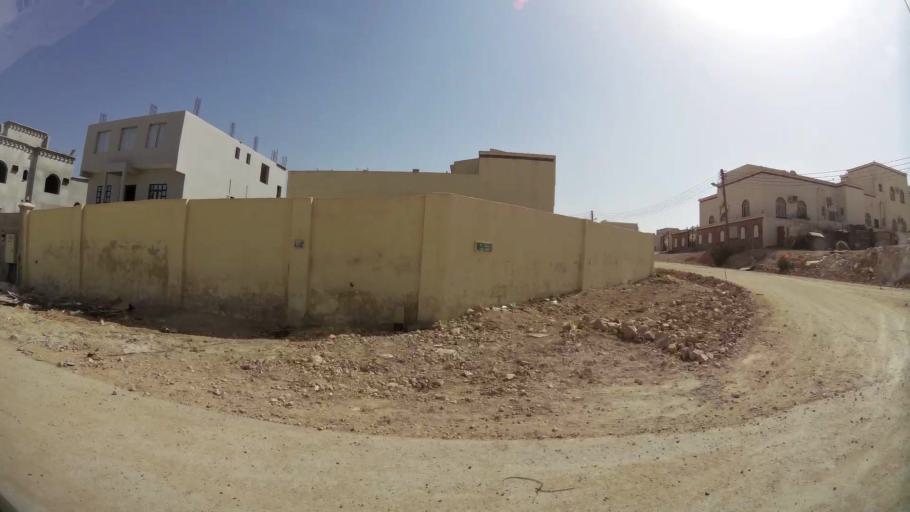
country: OM
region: Zufar
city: Salalah
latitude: 17.0032
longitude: 54.0198
